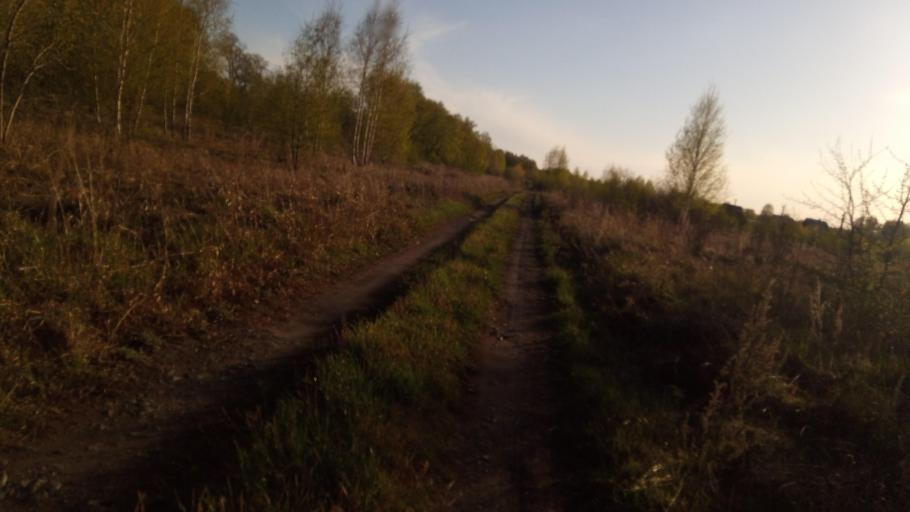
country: RU
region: Chelyabinsk
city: Timiryazevskiy
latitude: 54.9899
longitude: 60.8592
